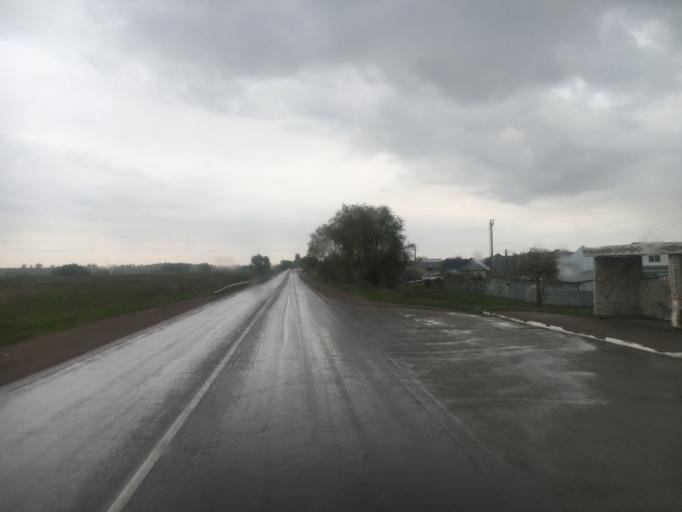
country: KZ
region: Almaty Oblysy
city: Burunday
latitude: 43.2910
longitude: 76.6733
